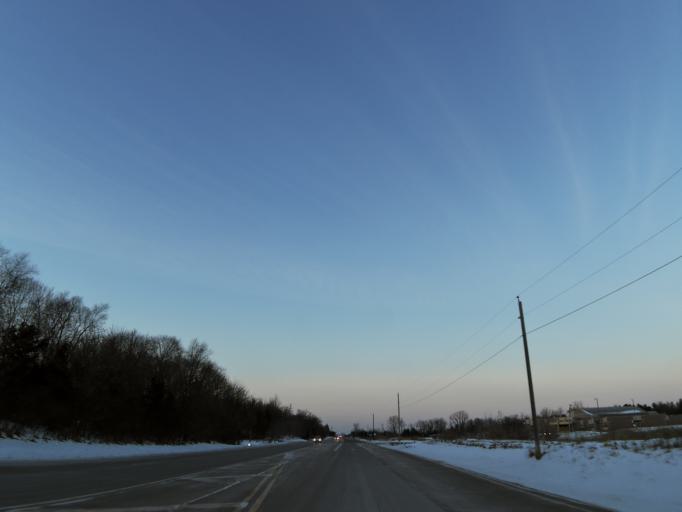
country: US
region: Minnesota
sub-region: Washington County
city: Lakeland
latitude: 44.9378
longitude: -92.7316
